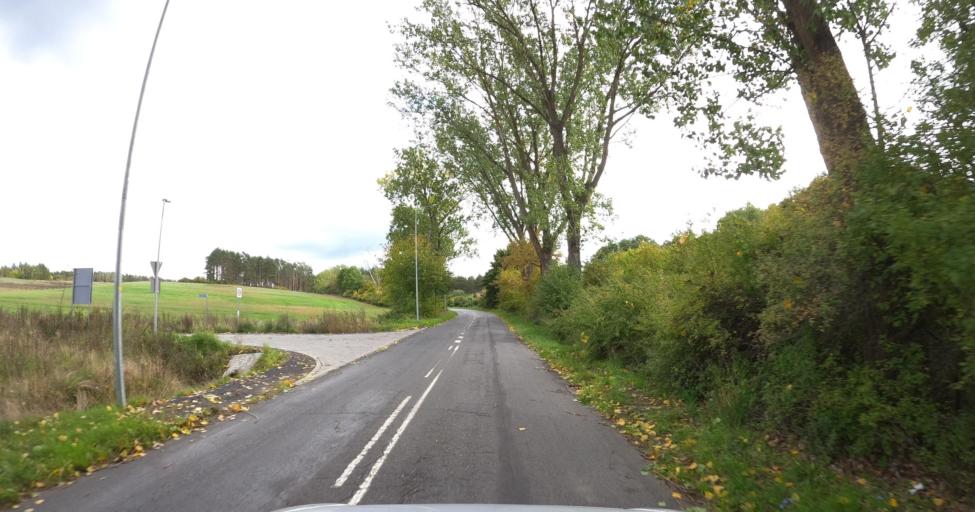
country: PL
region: Lubusz
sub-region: Powiat zielonogorski
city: Zabor
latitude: 51.9463
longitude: 15.6511
